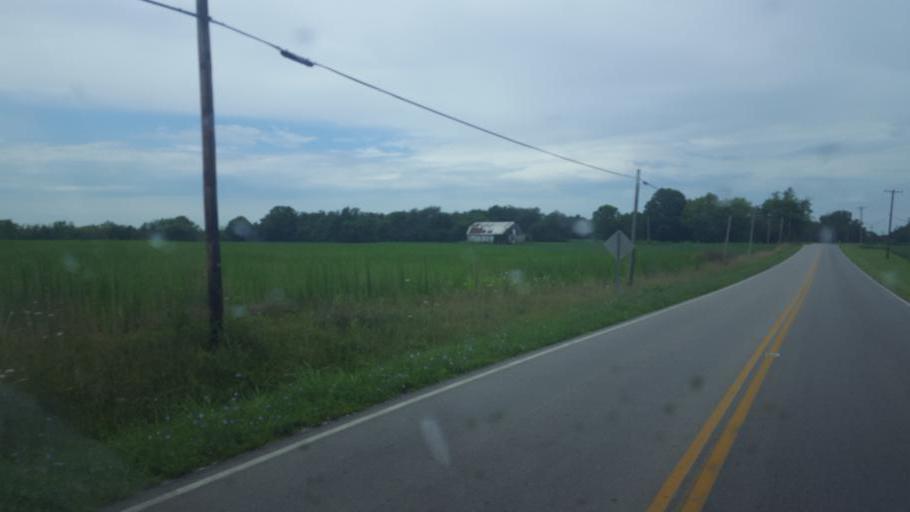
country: US
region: Ohio
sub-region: Pickaway County
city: Circleville
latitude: 39.6327
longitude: -82.9452
